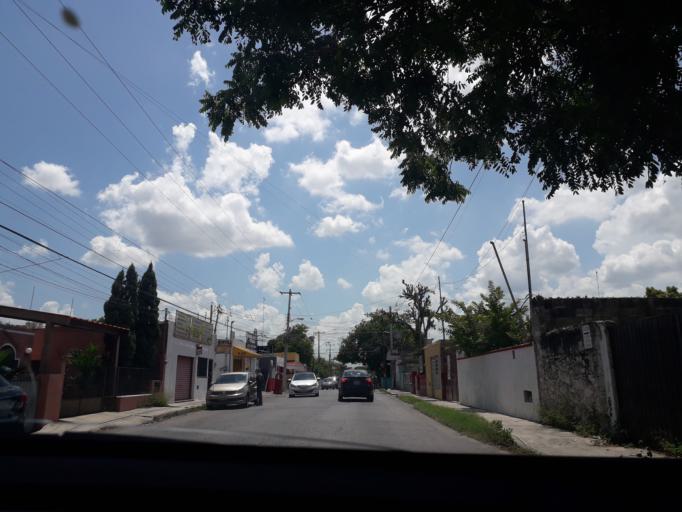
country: MX
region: Yucatan
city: Merida
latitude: 20.9641
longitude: -89.6474
